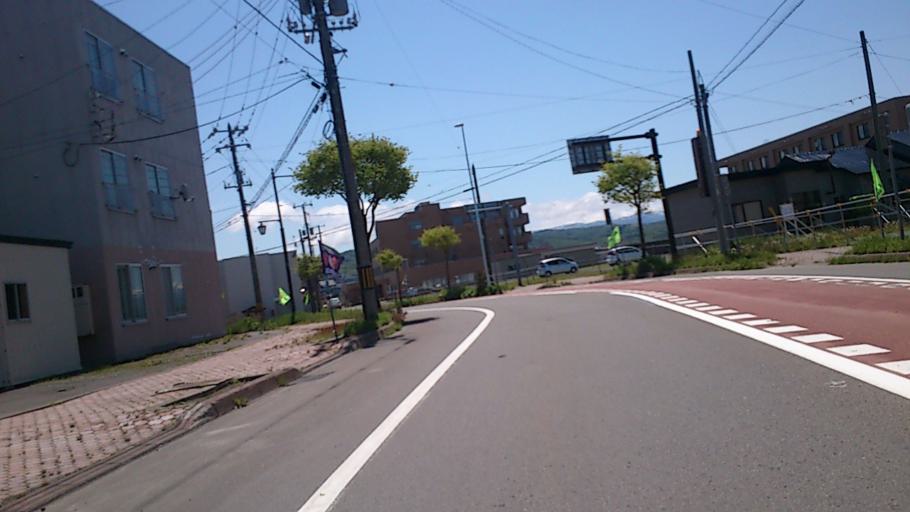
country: JP
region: Hokkaido
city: Rumoi
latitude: 43.9459
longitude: 141.6339
